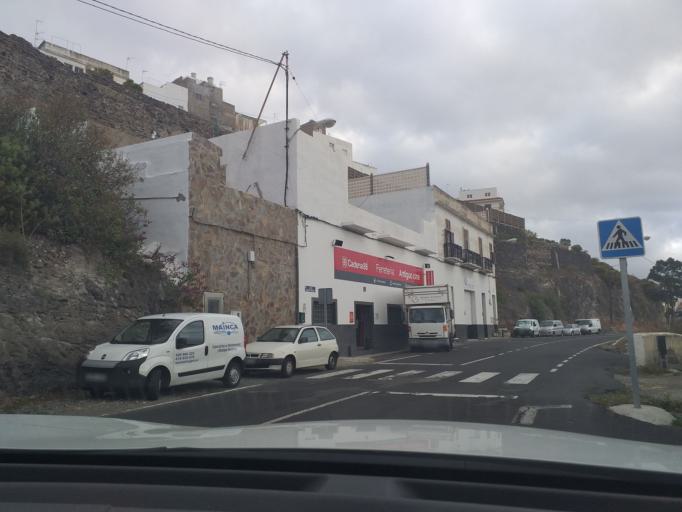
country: ES
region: Canary Islands
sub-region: Provincia de Las Palmas
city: Arucas
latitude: 28.1145
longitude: -15.4924
